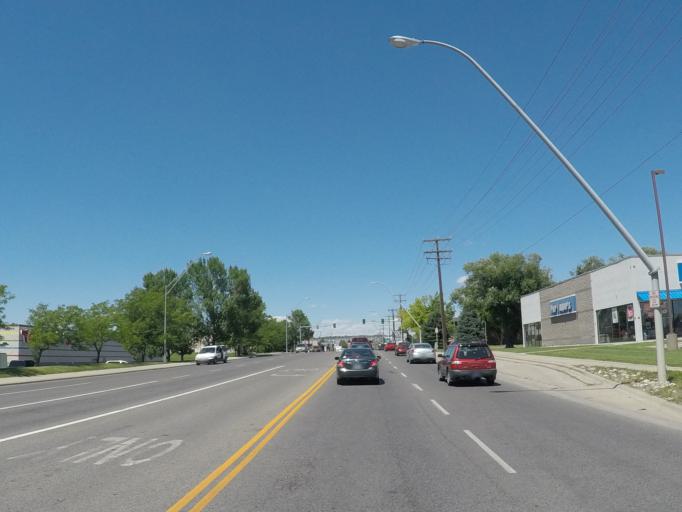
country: US
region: Montana
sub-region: Yellowstone County
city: Billings
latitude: 45.7572
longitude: -108.5762
